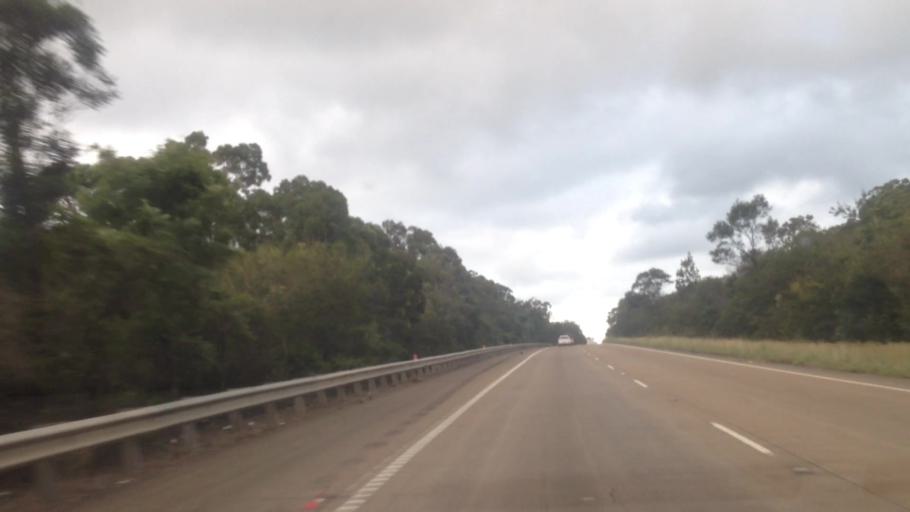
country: AU
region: New South Wales
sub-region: Lake Macquarie Shire
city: Dora Creek
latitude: -33.1545
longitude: 151.4712
